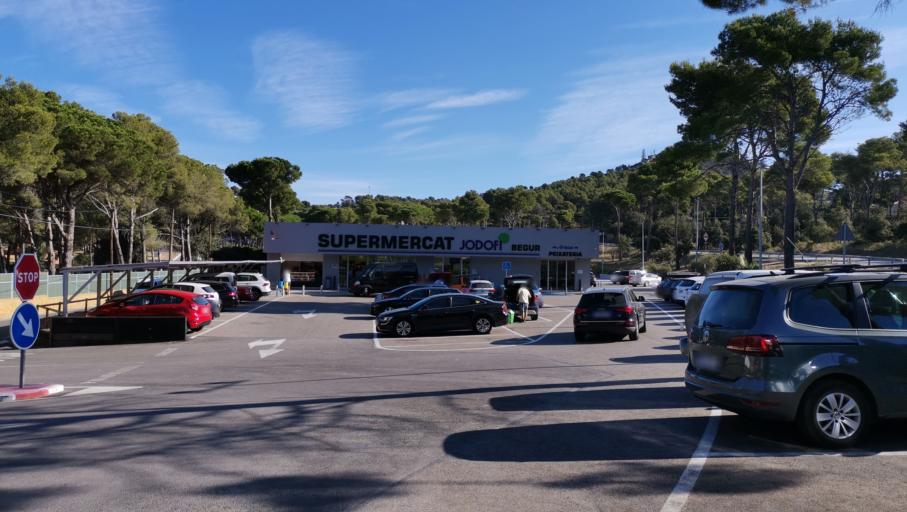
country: ES
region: Catalonia
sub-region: Provincia de Girona
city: Begur
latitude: 41.9406
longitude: 3.2011
